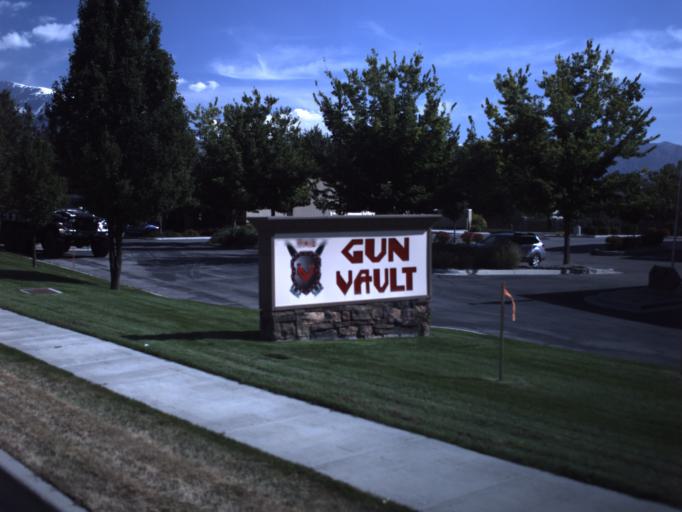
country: US
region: Utah
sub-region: Salt Lake County
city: South Jordan
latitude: 40.5620
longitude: -111.9275
